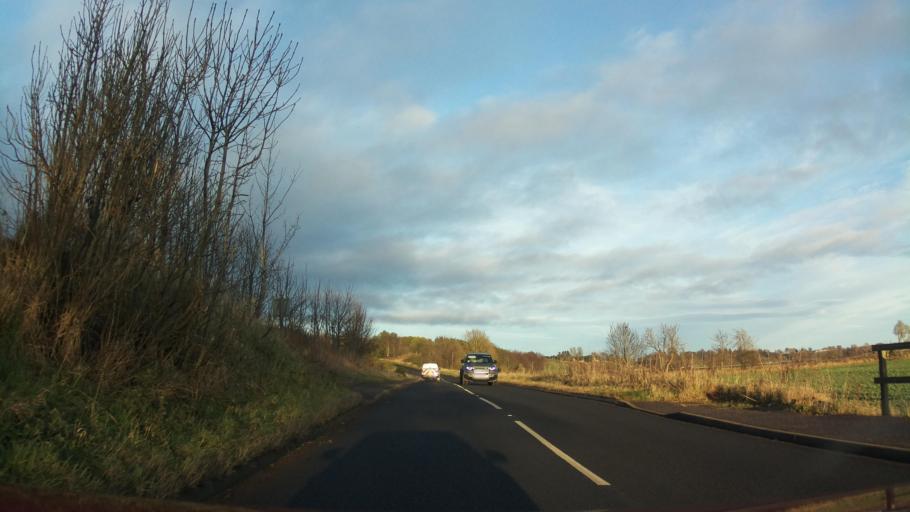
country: GB
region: Scotland
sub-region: Fife
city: Tayport
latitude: 56.4894
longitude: -2.8062
